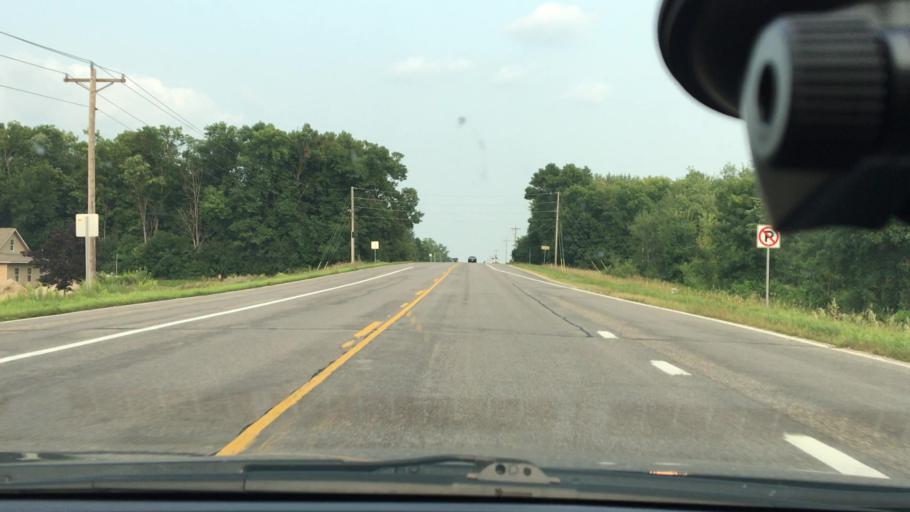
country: US
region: Minnesota
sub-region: Wright County
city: Albertville
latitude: 45.2897
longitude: -93.6755
